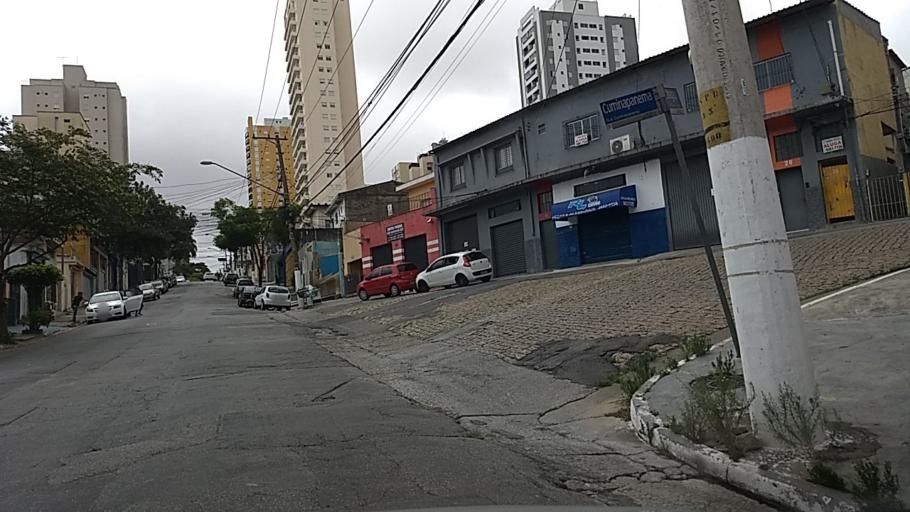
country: BR
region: Sao Paulo
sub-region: Sao Paulo
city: Sao Paulo
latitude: -23.6166
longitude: -46.6290
